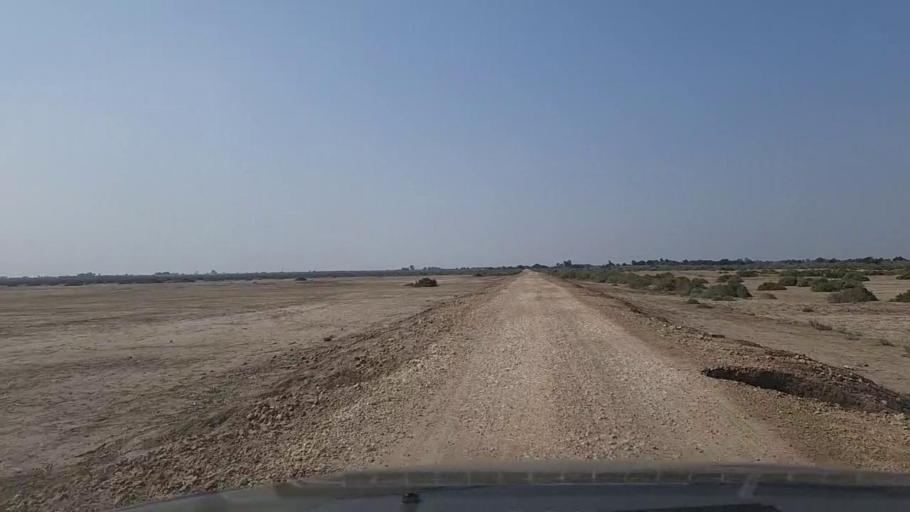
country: PK
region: Sindh
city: Mirpur Sakro
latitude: 24.4318
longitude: 67.7267
